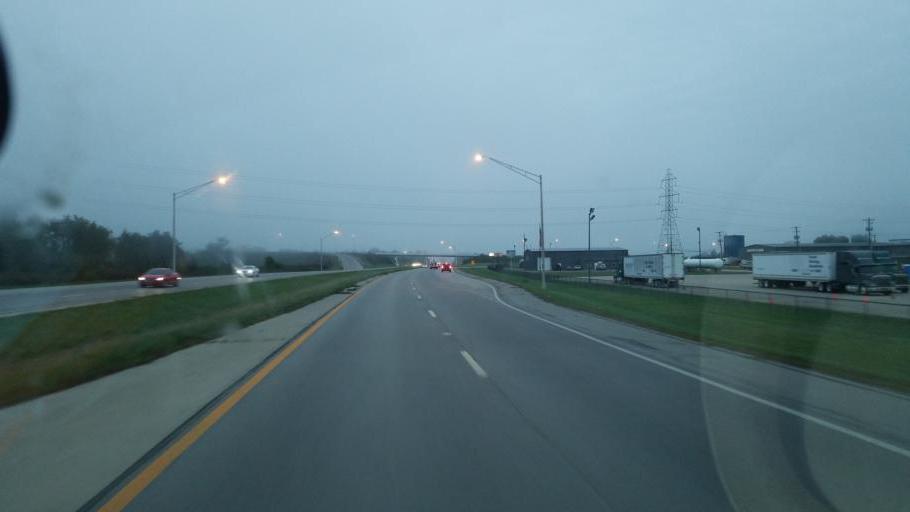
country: US
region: Ohio
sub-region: Pike County
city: Piketon
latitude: 39.0180
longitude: -83.0257
